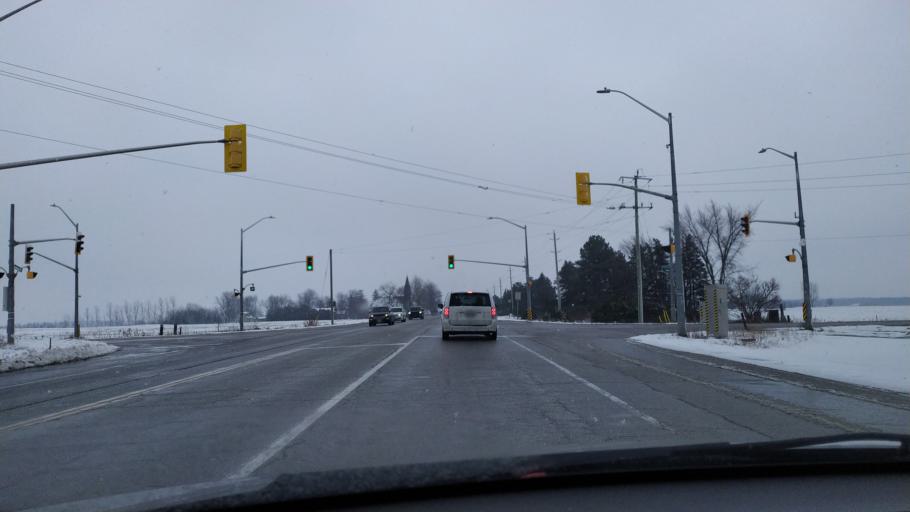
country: CA
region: Ontario
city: Waterloo
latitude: 43.6241
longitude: -80.6956
